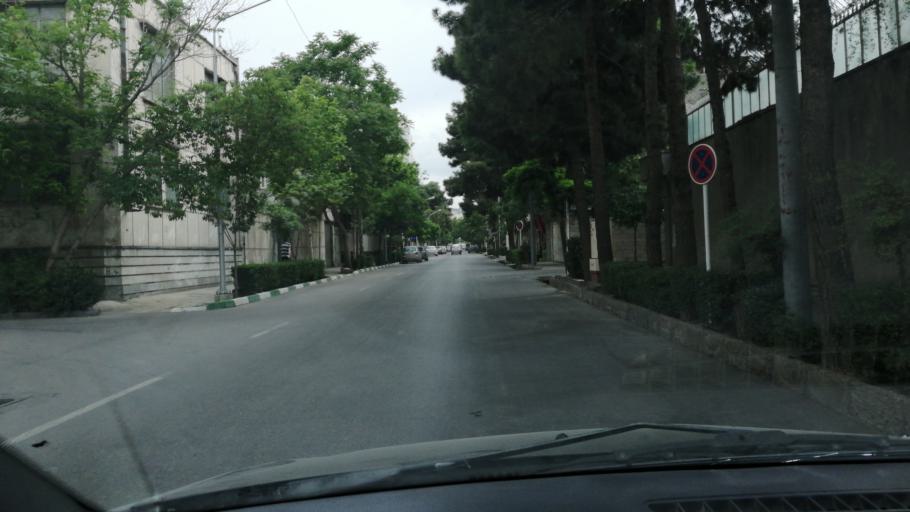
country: IR
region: Razavi Khorasan
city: Mashhad
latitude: 36.2877
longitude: 59.5850
